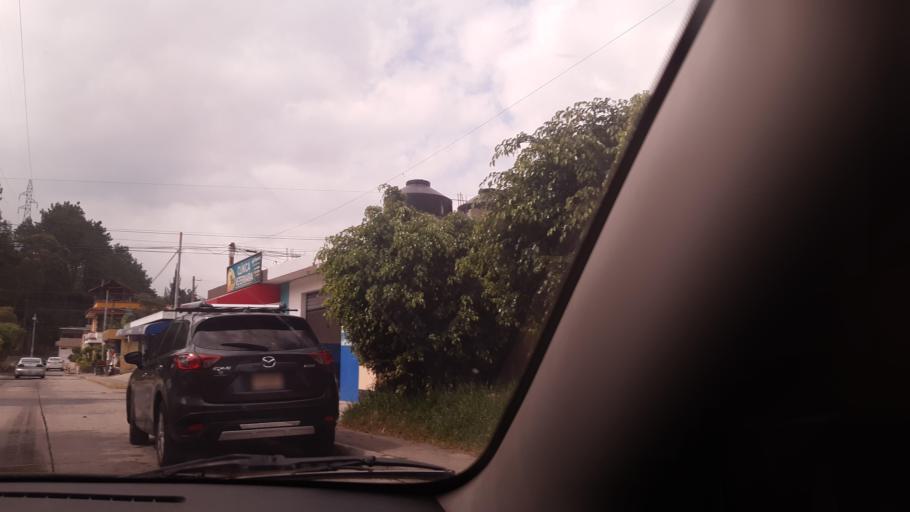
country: GT
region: Guatemala
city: Petapa
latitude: 14.5077
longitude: -90.5440
